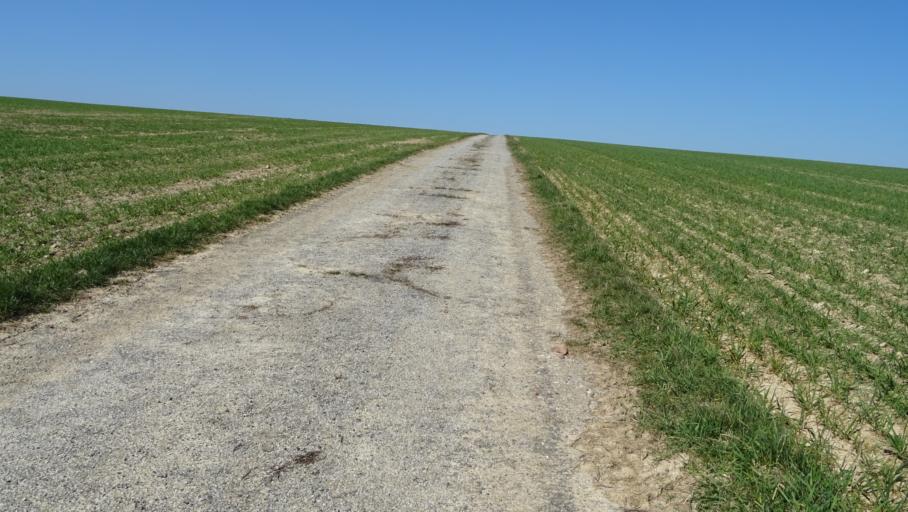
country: DE
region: Baden-Wuerttemberg
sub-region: Karlsruhe Region
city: Limbach
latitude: 49.4167
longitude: 9.2487
